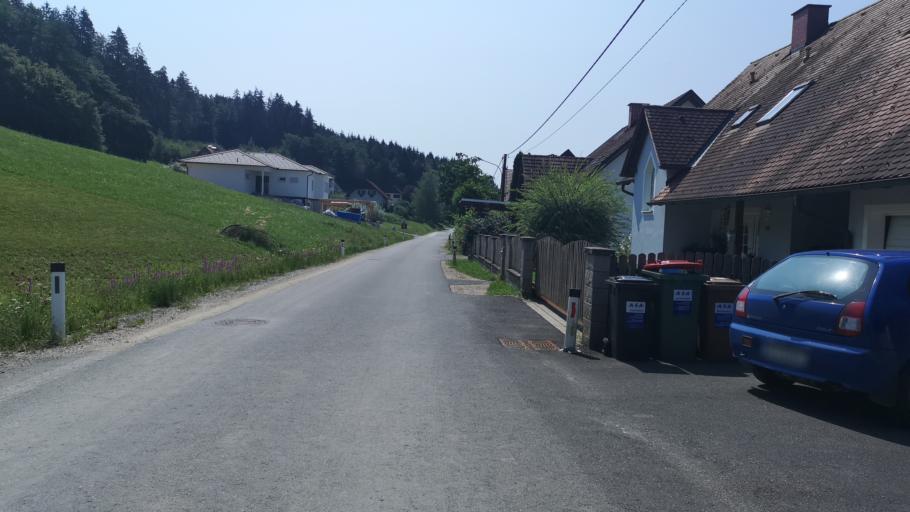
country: AT
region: Styria
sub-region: Politischer Bezirk Deutschlandsberg
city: Sankt Josef (Weststeiermark)
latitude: 46.8957
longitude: 15.3650
